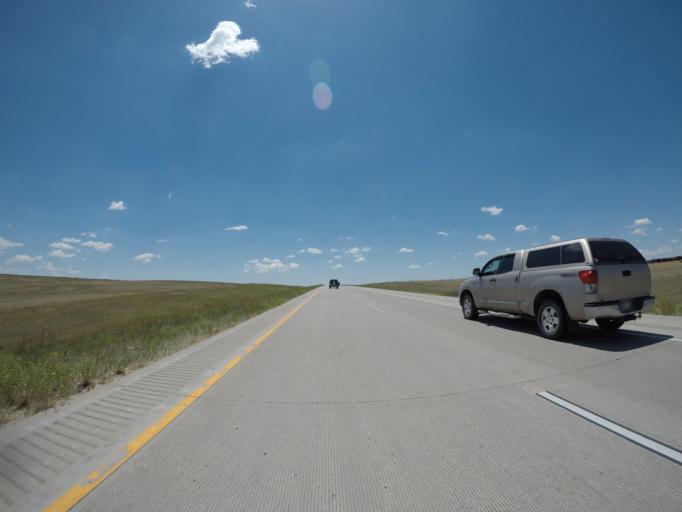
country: US
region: Colorado
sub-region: Lincoln County
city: Limon
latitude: 39.3955
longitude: -103.8965
